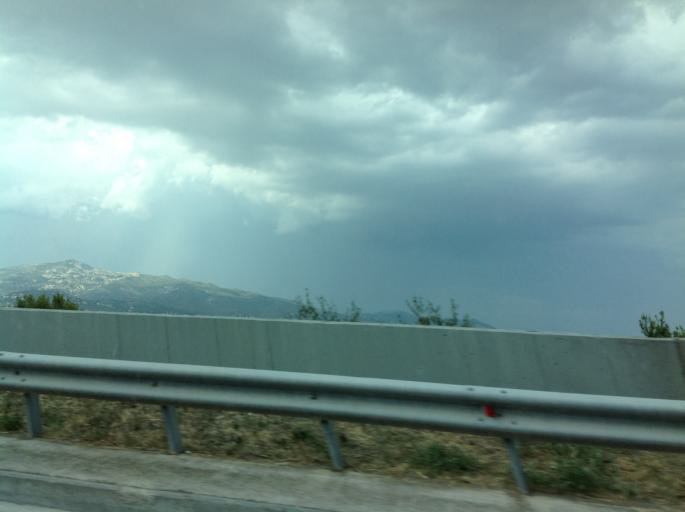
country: GR
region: Attica
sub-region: Nomarchia Athinas
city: Agia Paraskevi
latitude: 38.0041
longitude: 23.8454
